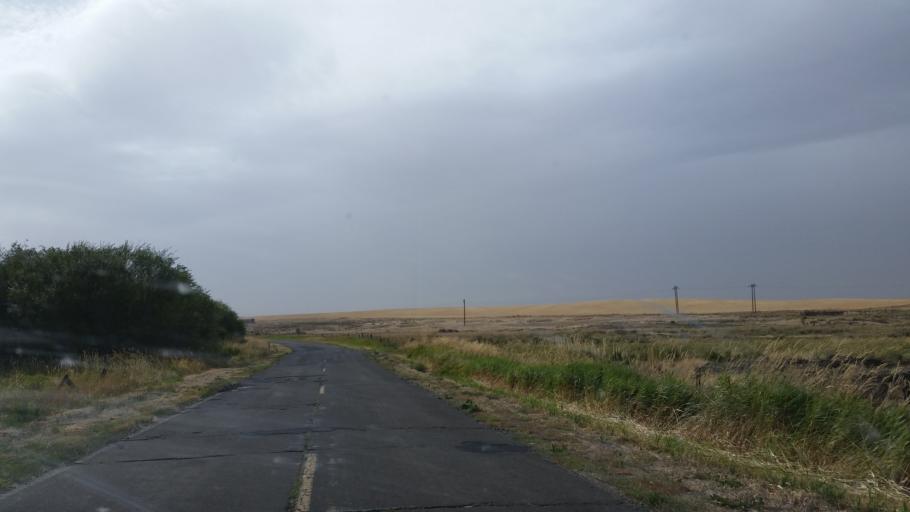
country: US
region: Washington
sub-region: Lincoln County
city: Davenport
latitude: 47.6658
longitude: -117.9254
